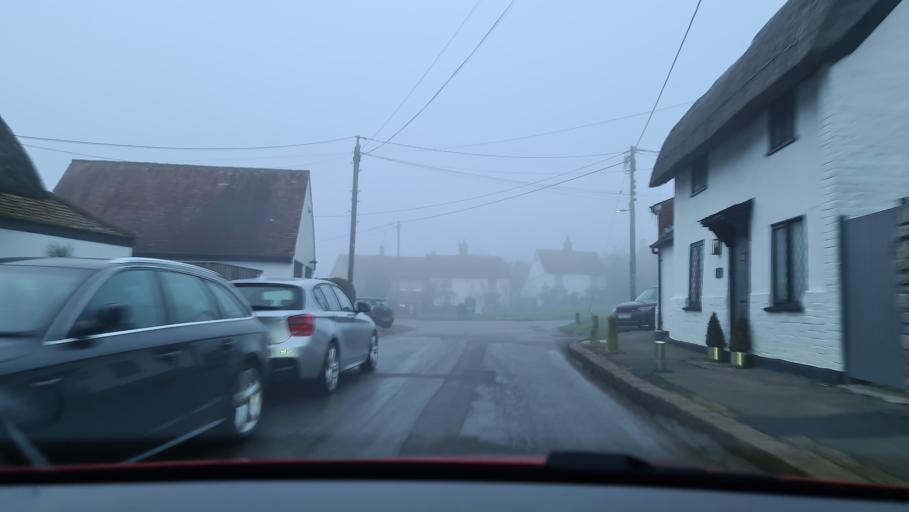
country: GB
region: England
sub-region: Buckinghamshire
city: Waddesdon
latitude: 51.8738
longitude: -0.9162
